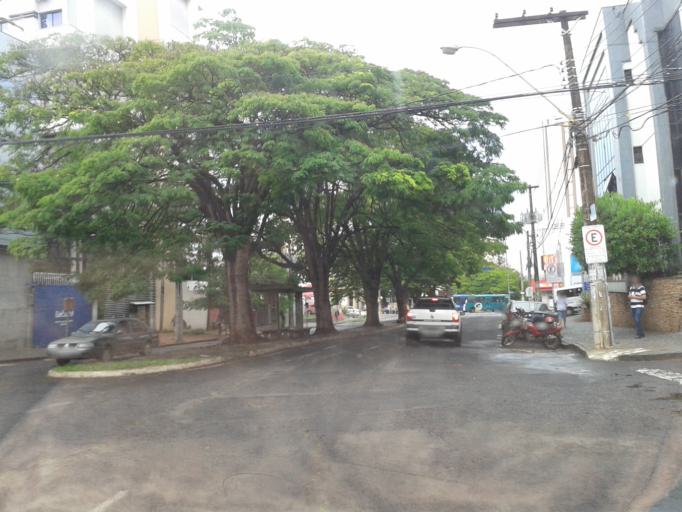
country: BR
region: Minas Gerais
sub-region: Uberlandia
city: Uberlandia
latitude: -18.9167
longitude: -48.2809
